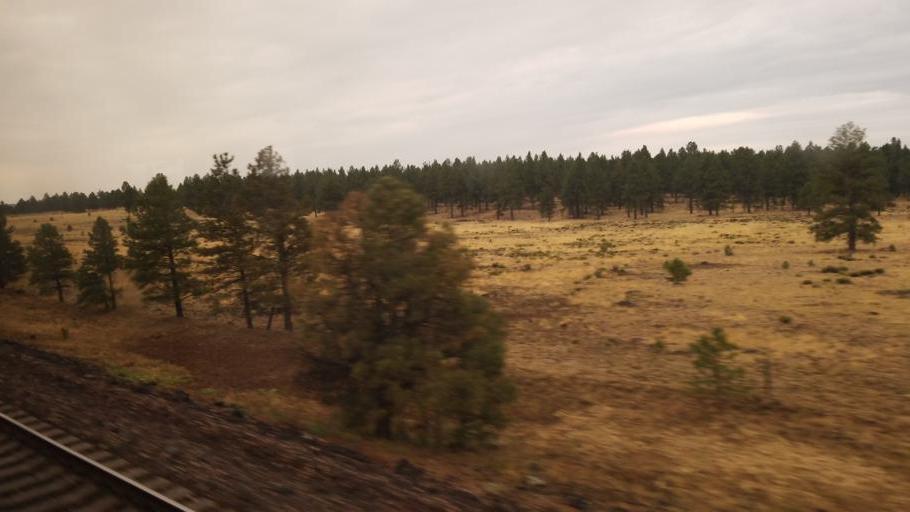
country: US
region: Arizona
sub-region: Coconino County
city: Parks
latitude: 35.2414
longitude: -111.9869
